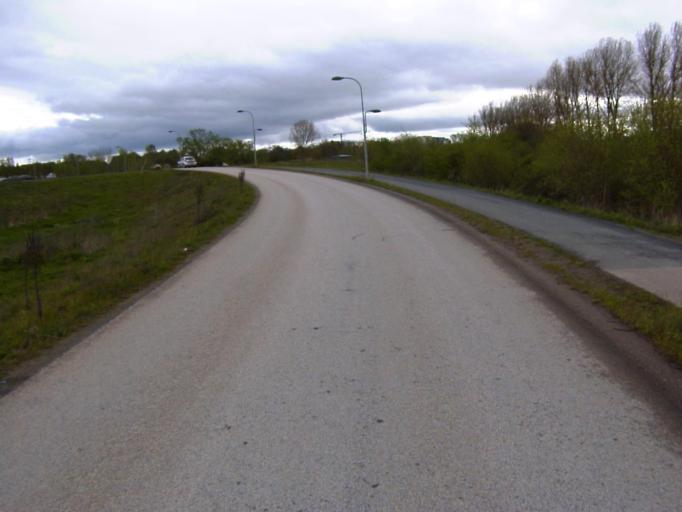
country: SE
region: Skane
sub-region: Kristianstads Kommun
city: Kristianstad
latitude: 56.0250
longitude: 14.1431
